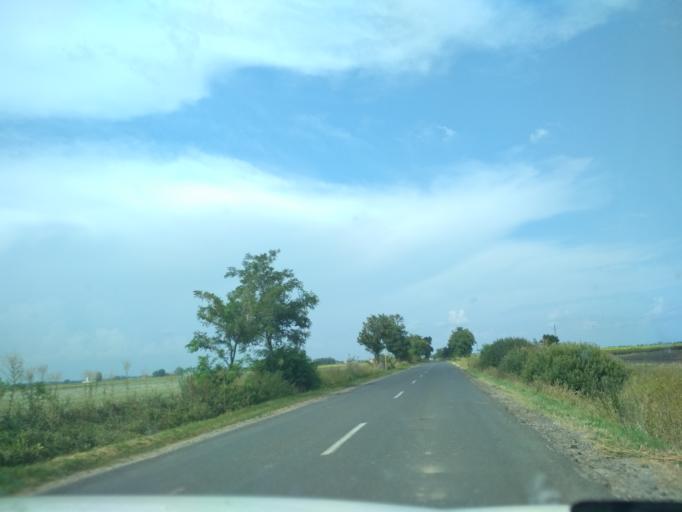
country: HU
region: Jasz-Nagykun-Szolnok
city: Tiszaszolos
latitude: 47.5344
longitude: 20.7142
